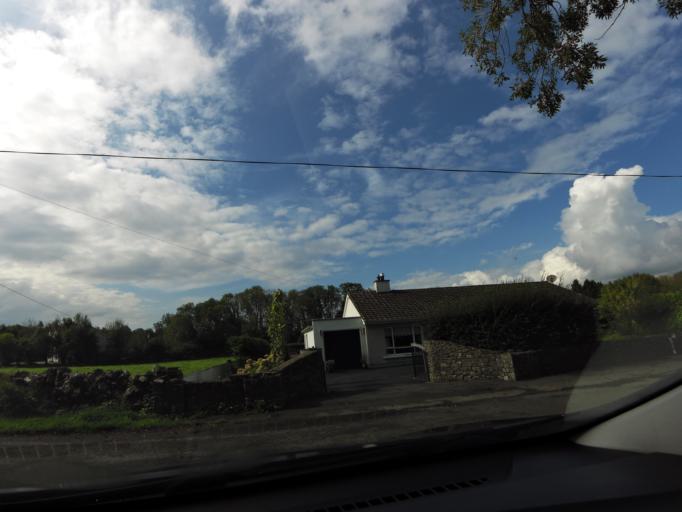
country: IE
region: Connaught
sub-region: County Galway
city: Athenry
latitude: 53.2564
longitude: -8.8132
